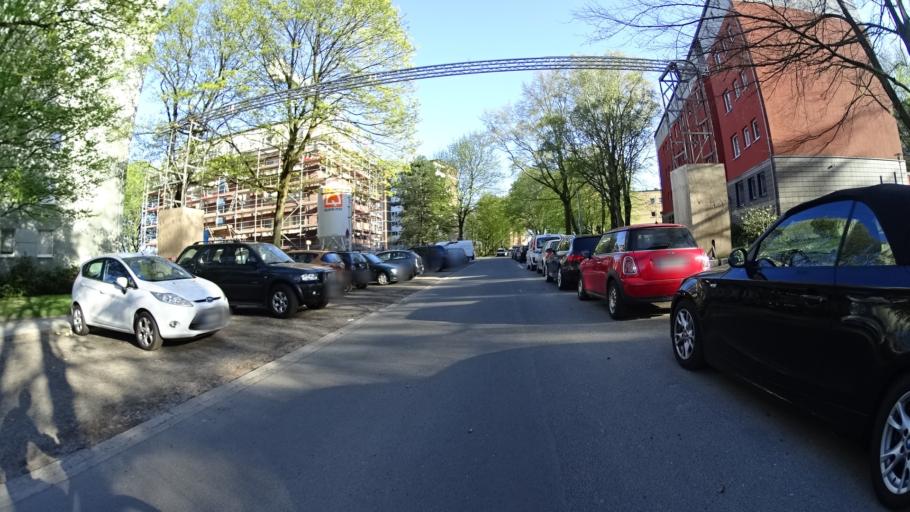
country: DE
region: Hamburg
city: Stellingen
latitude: 53.5908
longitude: 9.9373
